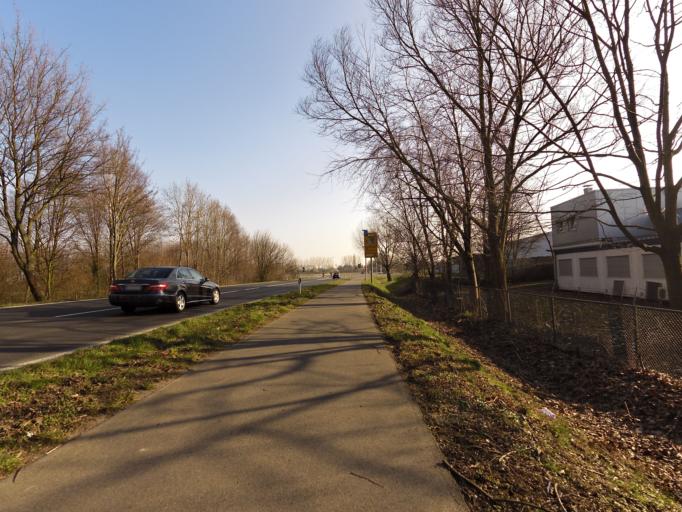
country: DE
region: North Rhine-Westphalia
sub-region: Regierungsbezirk Dusseldorf
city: Emmerich
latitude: 51.8398
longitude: 6.2757
